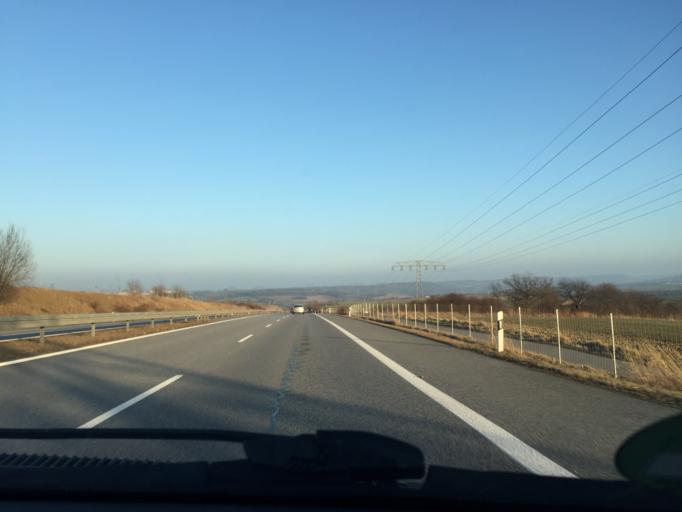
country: DE
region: Saxony
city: Dohna
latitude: 50.9462
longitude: 13.8888
